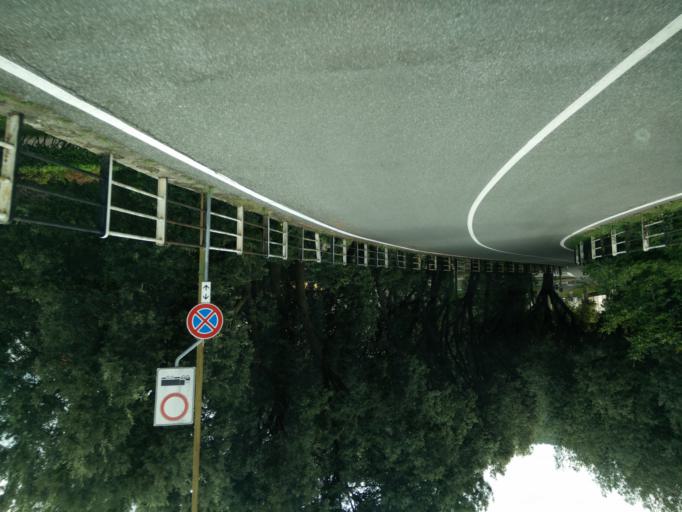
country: IT
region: Tuscany
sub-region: Provincia di Massa-Carrara
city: Fivizzano
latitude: 44.2353
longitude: 10.1229
